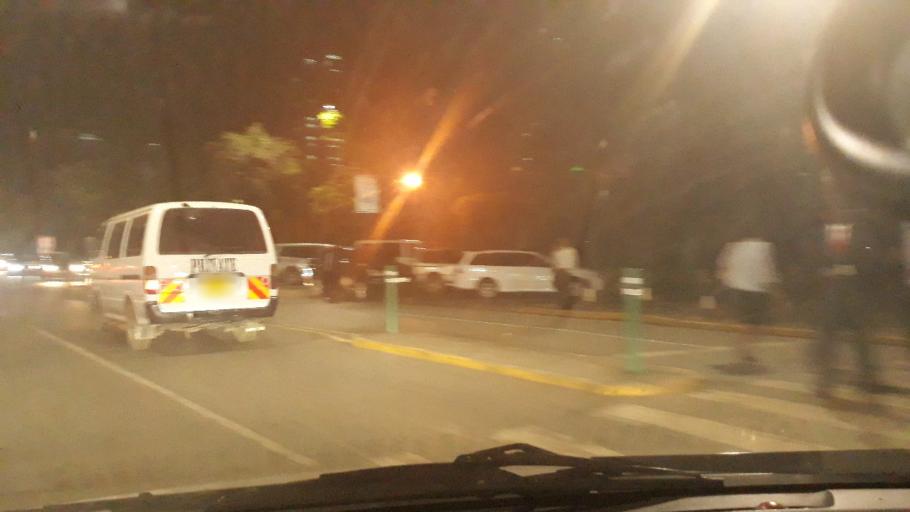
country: KE
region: Nairobi Area
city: Nairobi
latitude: -1.2863
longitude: 36.8237
